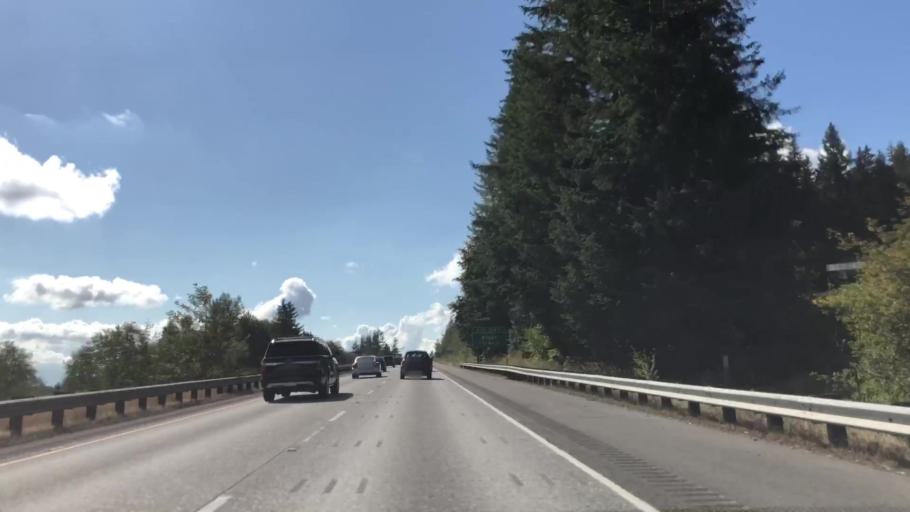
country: US
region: Washington
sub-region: Whatcom County
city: Sudden Valley
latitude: 48.6339
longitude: -122.3583
